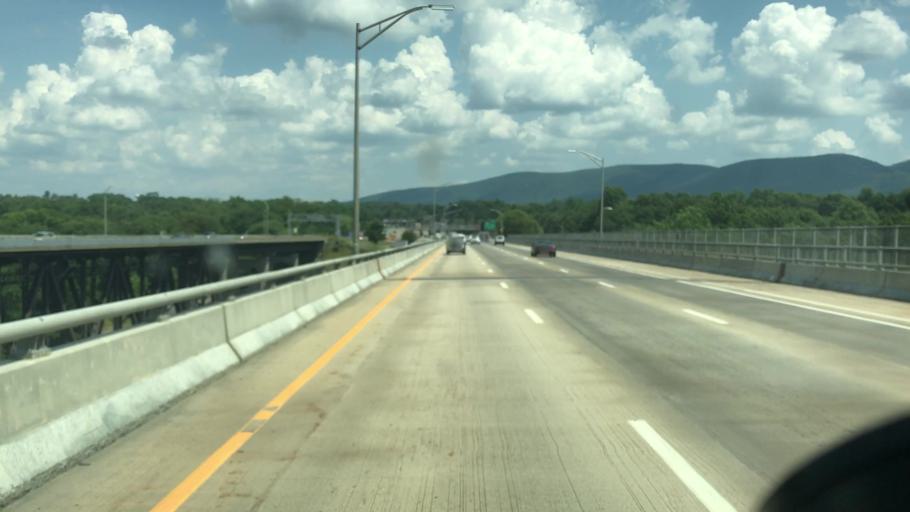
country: US
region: New York
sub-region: Dutchess County
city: Beacon
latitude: 41.5184
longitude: -73.9855
